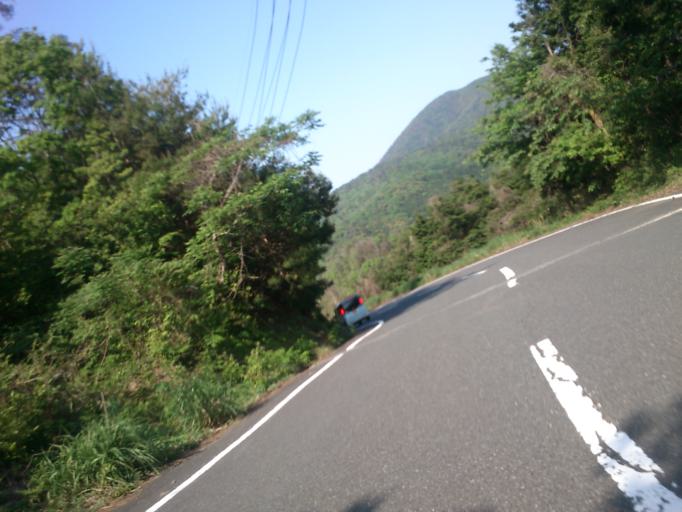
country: JP
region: Kyoto
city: Miyazu
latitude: 35.7408
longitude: 135.1745
